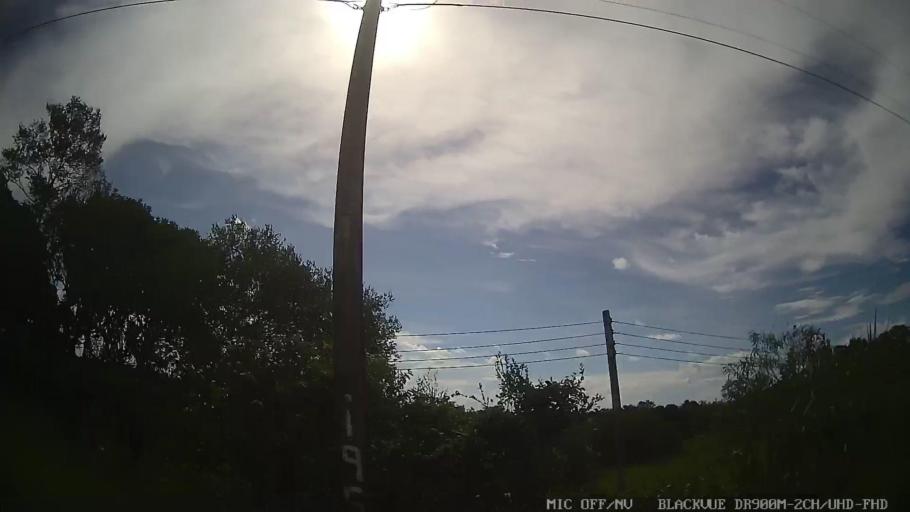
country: BR
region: Sao Paulo
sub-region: Conchas
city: Conchas
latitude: -22.9966
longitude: -47.9999
